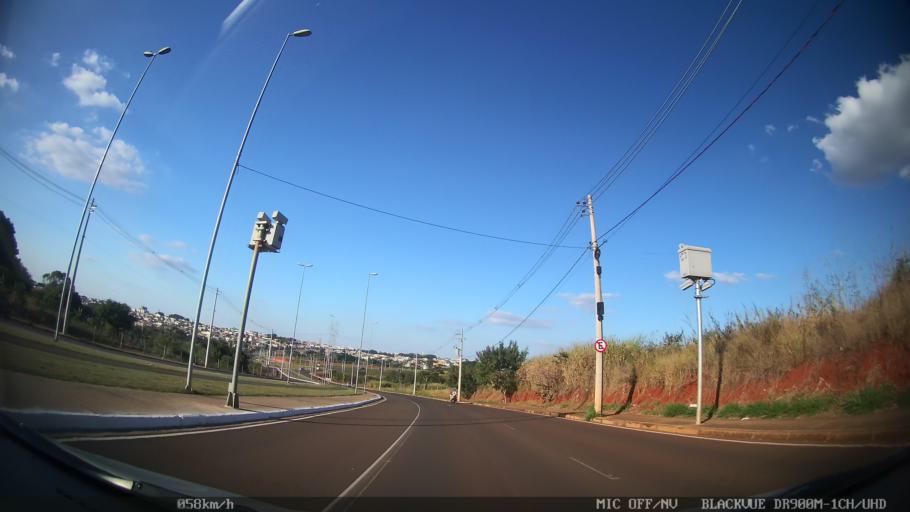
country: BR
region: Sao Paulo
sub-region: Santa Barbara D'Oeste
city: Santa Barbara d'Oeste
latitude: -22.7457
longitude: -47.3922
